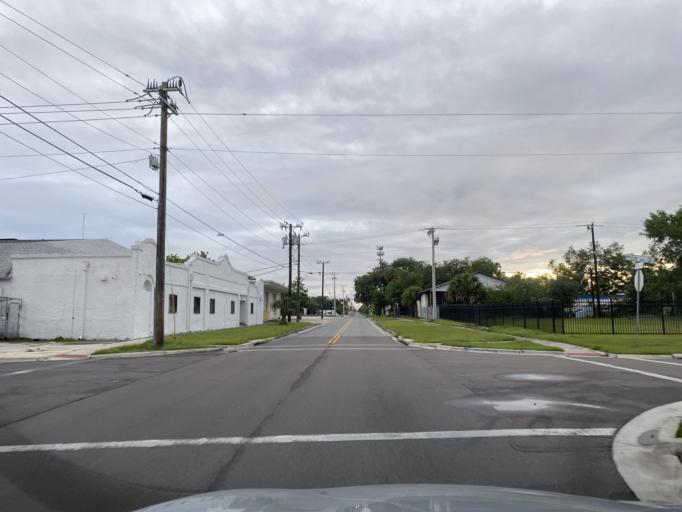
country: US
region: Florida
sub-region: Seminole County
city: Sanford
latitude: 28.8008
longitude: -81.2708
